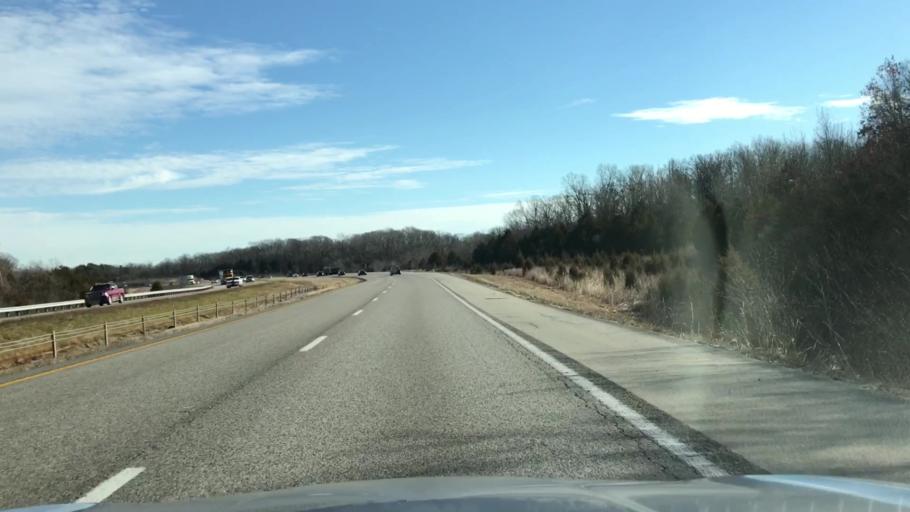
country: US
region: Missouri
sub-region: Montgomery County
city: Montgomery City
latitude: 38.8953
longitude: -91.6278
